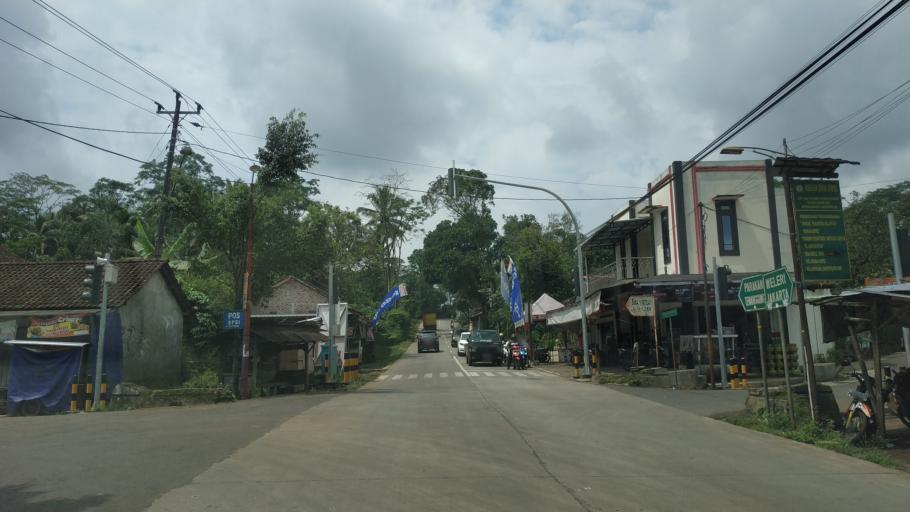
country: ID
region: Central Java
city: Weleri
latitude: -7.0985
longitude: 110.0627
